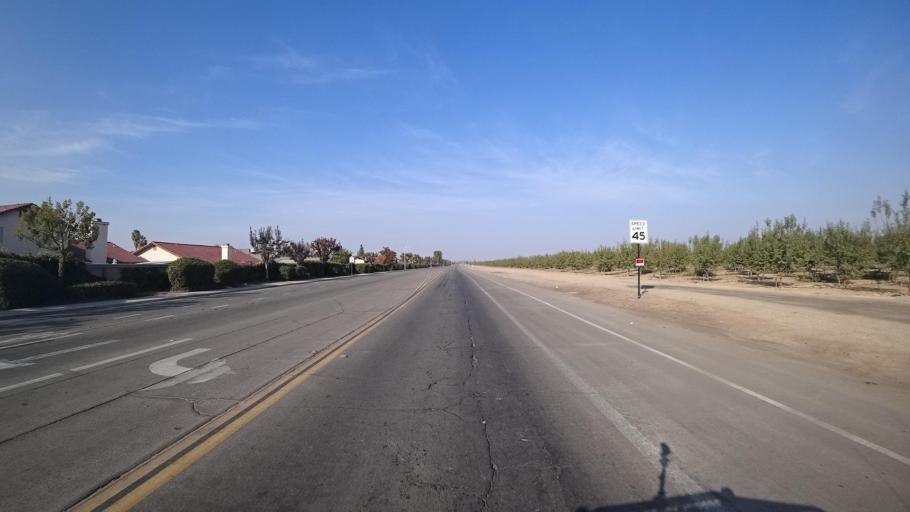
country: US
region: California
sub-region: Kern County
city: Delano
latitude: 35.7761
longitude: -119.2231
